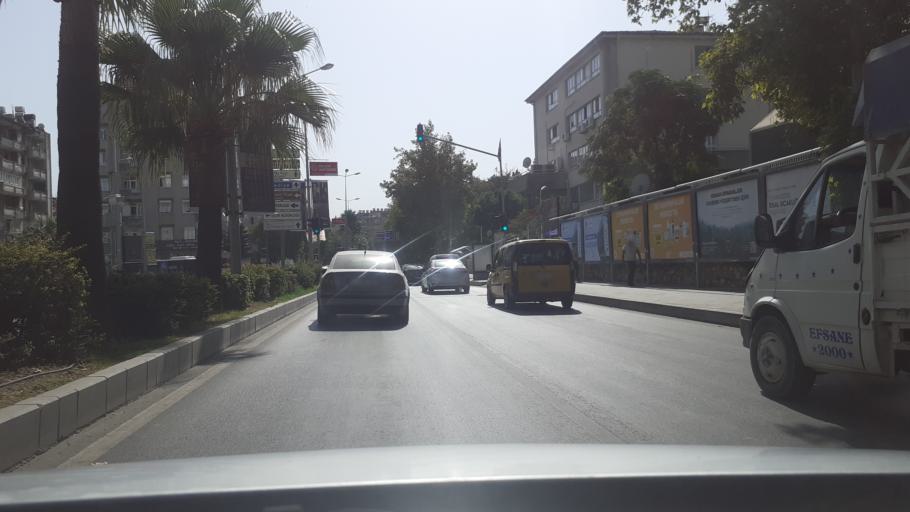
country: TR
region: Hatay
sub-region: Antakya Ilcesi
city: Antakya
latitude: 36.2115
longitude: 36.1597
